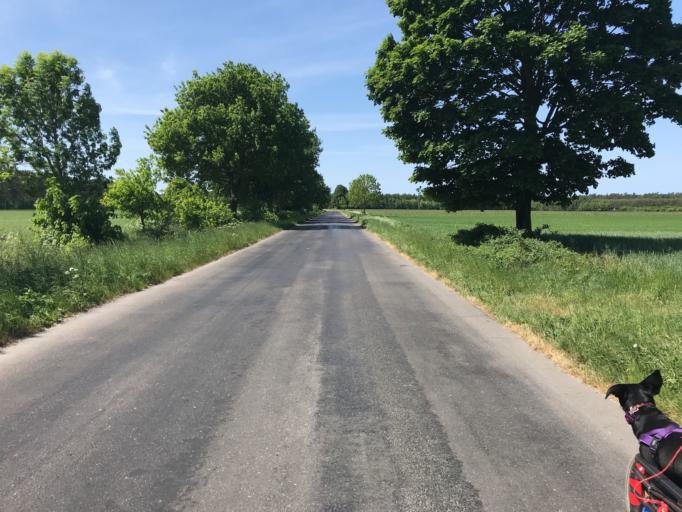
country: PL
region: West Pomeranian Voivodeship
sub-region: Powiat kamienski
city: Wolin
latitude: 53.7622
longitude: 14.6796
